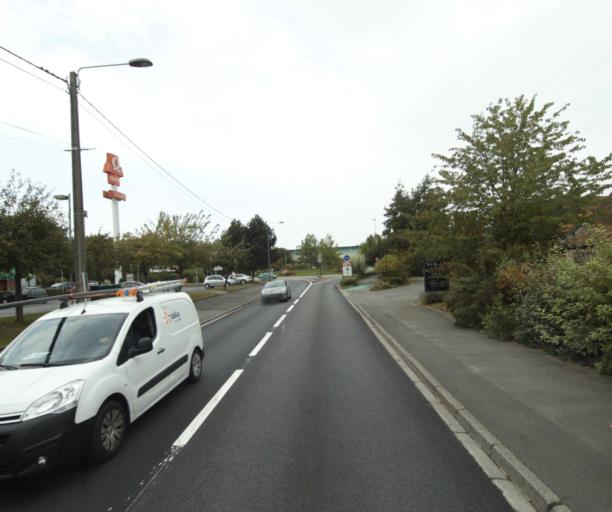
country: FR
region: Nord-Pas-de-Calais
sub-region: Departement du Nord
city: Lambersart
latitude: 50.6658
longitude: 3.0300
